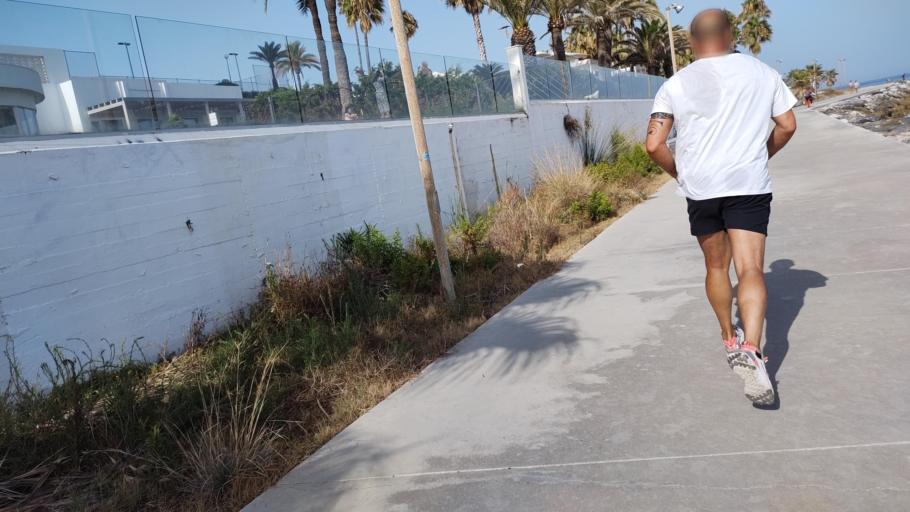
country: ES
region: Andalusia
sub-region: Provincia de Malaga
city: Benalmadena
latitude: 36.5794
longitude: -4.5415
